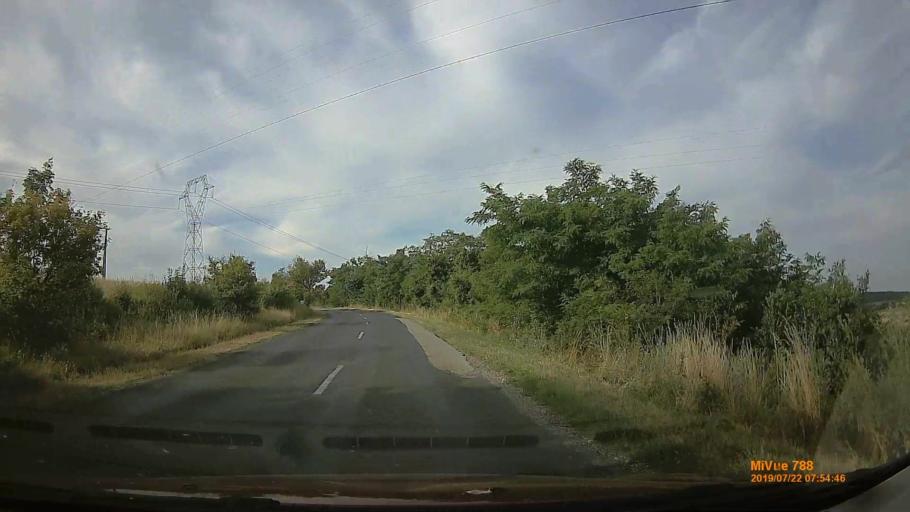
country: HU
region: Veszprem
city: Ajka
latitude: 47.0370
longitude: 17.5568
